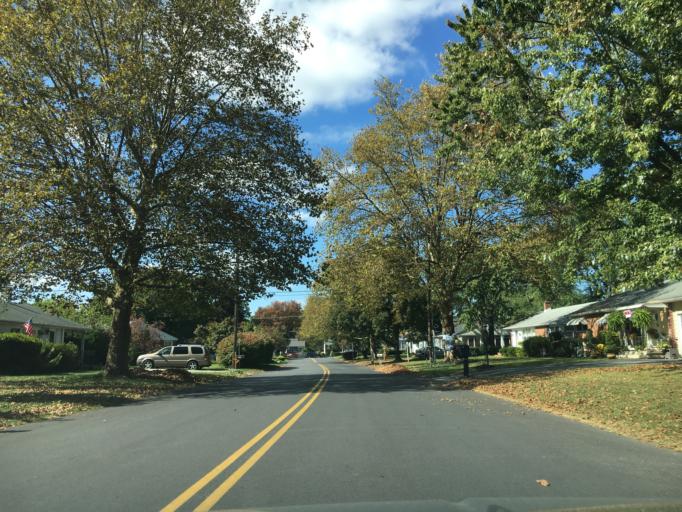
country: US
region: Pennsylvania
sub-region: York County
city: East York
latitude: 39.9674
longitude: -76.6782
